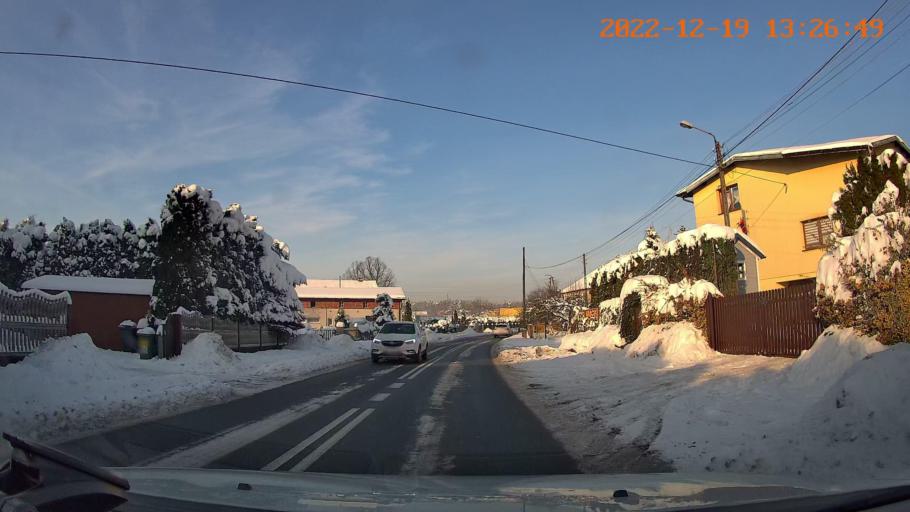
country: PL
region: Silesian Voivodeship
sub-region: Powiat bierunsko-ledzinski
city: Ledziny
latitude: 50.1037
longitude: 19.1366
